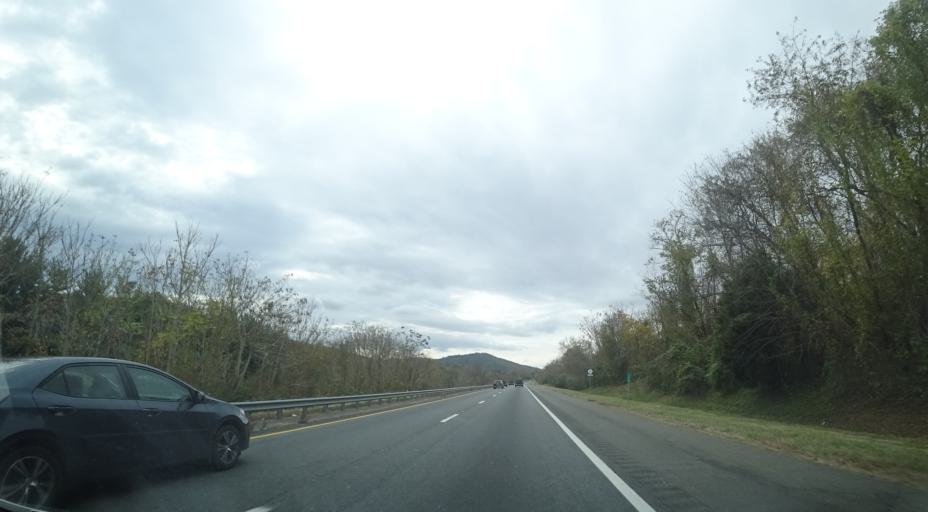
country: US
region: Virginia
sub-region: Warren County
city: Apple Mountain Lake
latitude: 38.9071
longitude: -78.0081
